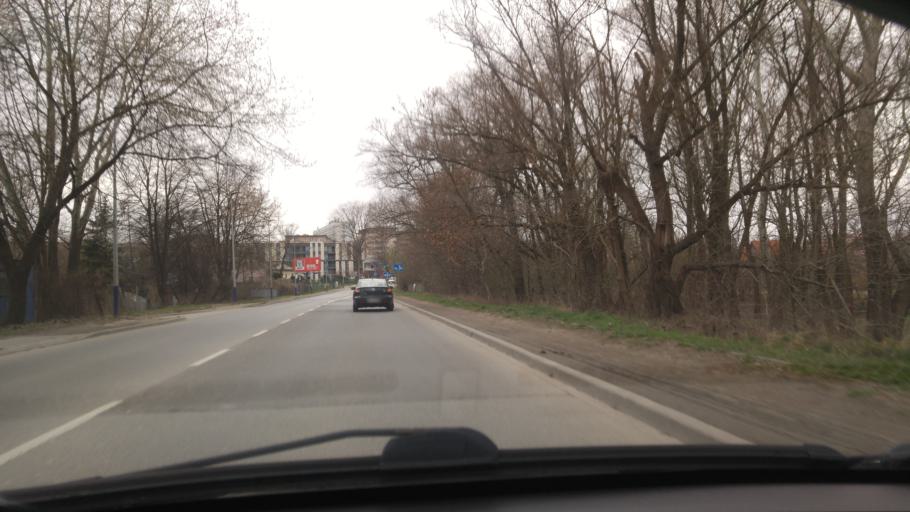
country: PL
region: Lesser Poland Voivodeship
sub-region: Powiat krakowski
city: Michalowice
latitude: 50.0933
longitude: 20.0307
